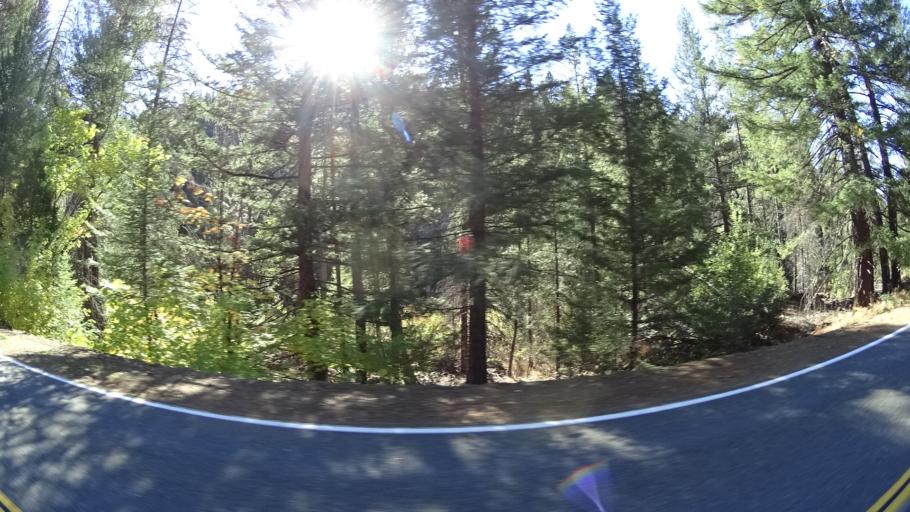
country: US
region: California
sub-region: Trinity County
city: Weaverville
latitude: 41.1855
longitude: -123.0782
